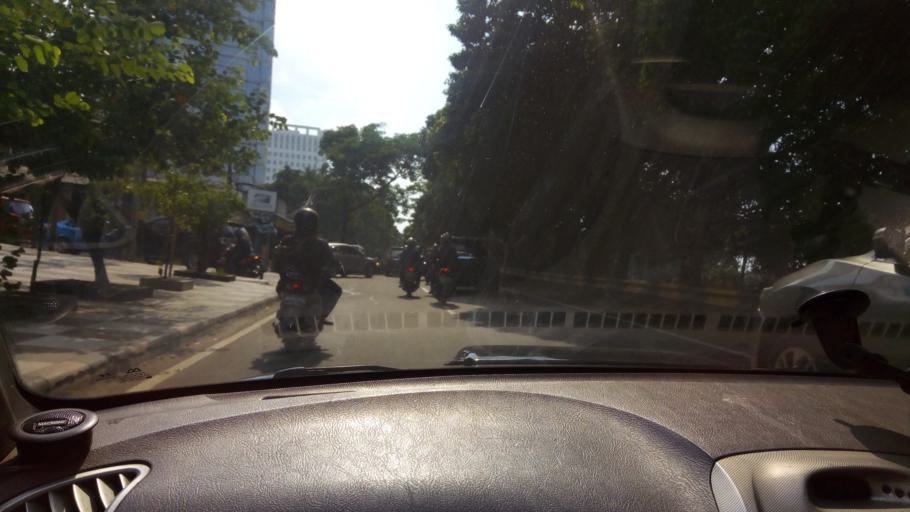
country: ID
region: Jakarta Raya
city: Jakarta
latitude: -6.2985
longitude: 106.8338
